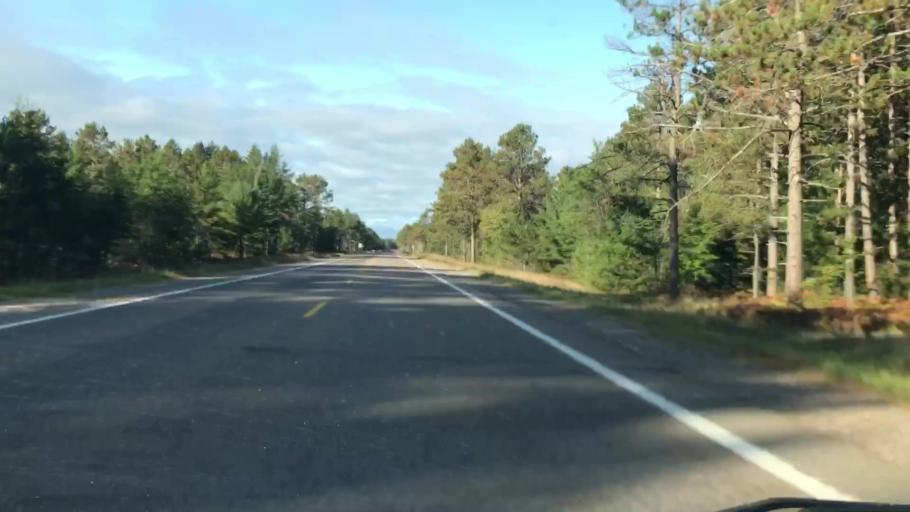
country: US
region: Michigan
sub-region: Mackinac County
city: Saint Ignace
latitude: 46.3535
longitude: -84.9011
